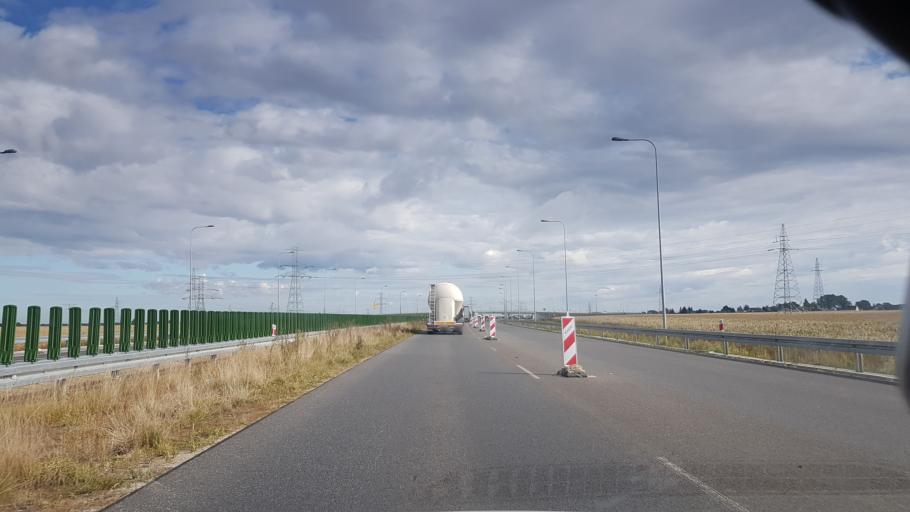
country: PL
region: Greater Poland Voivodeship
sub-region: Powiat poznanski
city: Steszew
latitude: 52.3297
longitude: 16.7263
